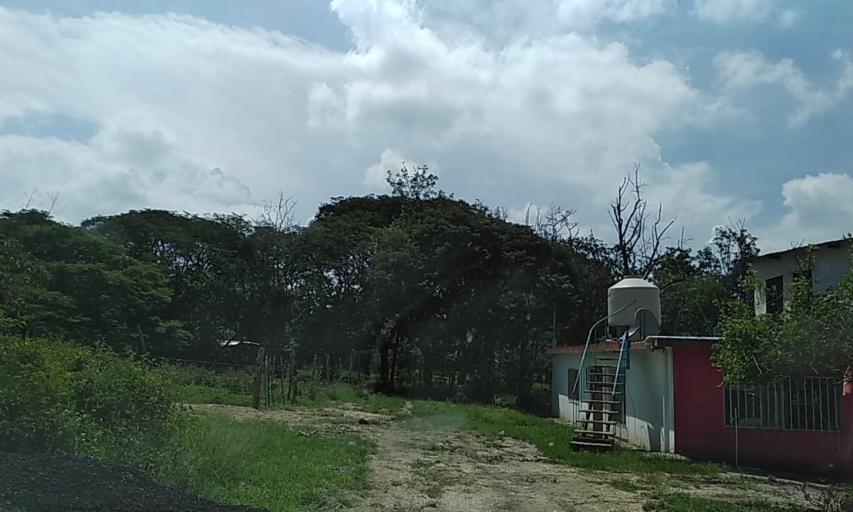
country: MX
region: Veracruz
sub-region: Emiliano Zapata
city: Dos Rios
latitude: 19.4421
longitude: -96.7813
